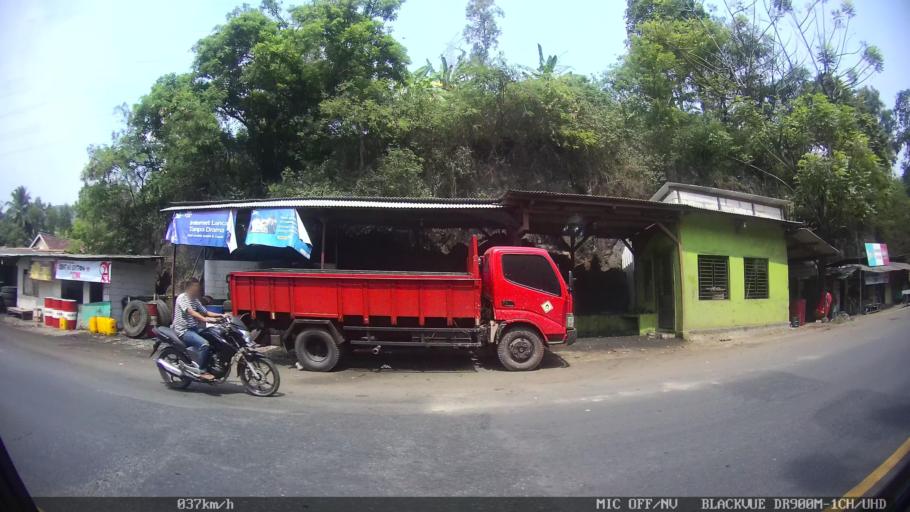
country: ID
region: Banten
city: Curug
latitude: -5.9451
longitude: 106.0045
